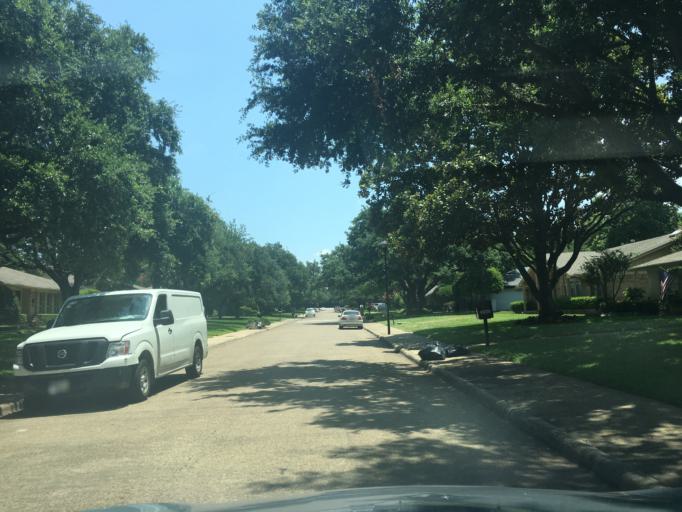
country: US
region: Texas
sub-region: Dallas County
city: Addison
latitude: 32.9198
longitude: -96.8416
